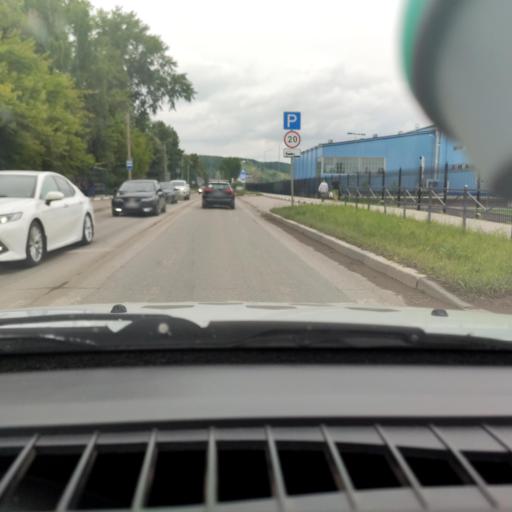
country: RU
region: Perm
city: Kungur
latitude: 57.4360
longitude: 56.9519
